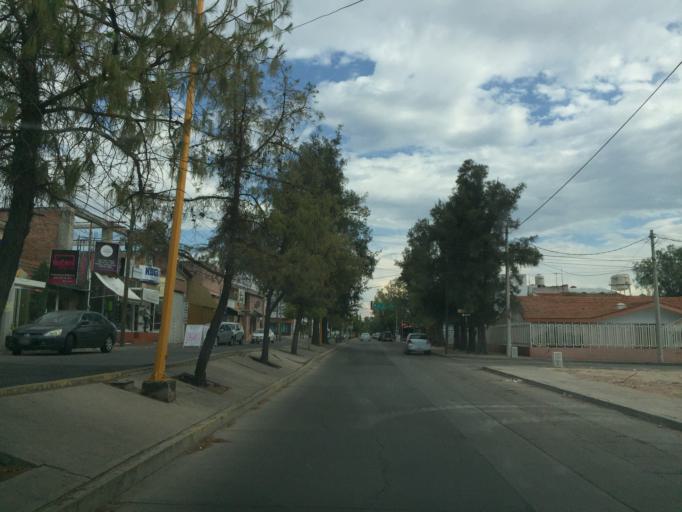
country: MX
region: Aguascalientes
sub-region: Jesus Maria
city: El Llano
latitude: 21.9237
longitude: -102.3047
